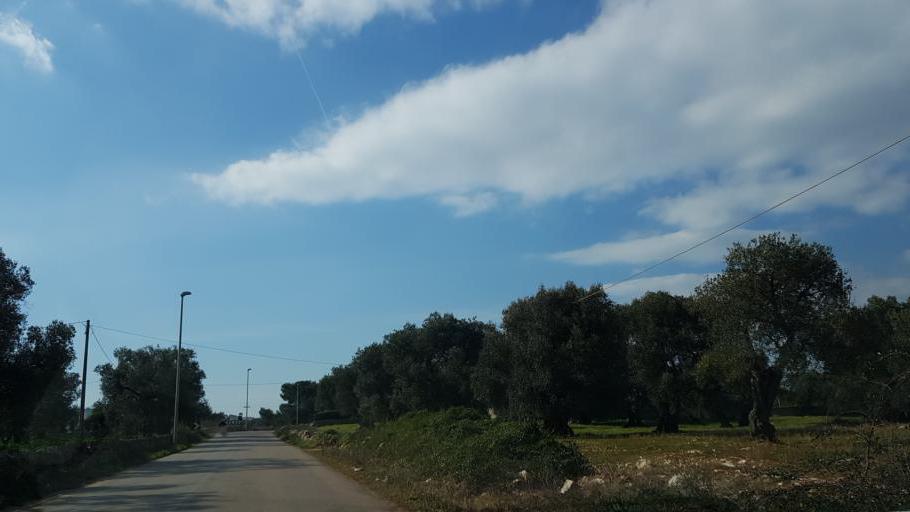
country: IT
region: Apulia
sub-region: Provincia di Brindisi
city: Carovigno
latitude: 40.7113
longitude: 17.6730
